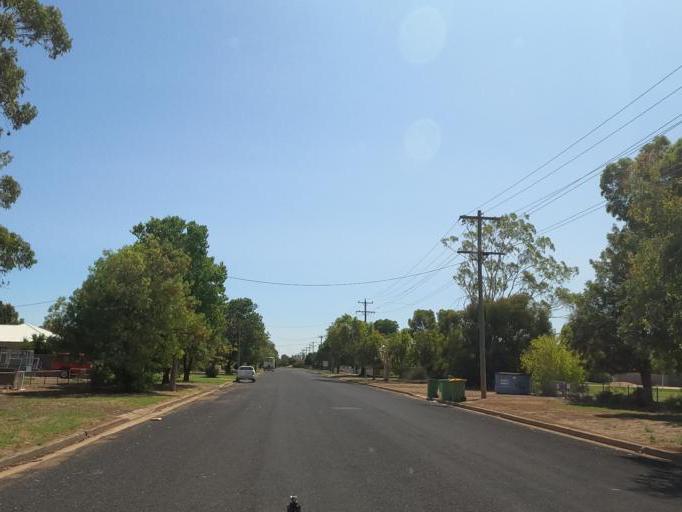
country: AU
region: New South Wales
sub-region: Corowa Shire
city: Mulwala
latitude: -35.9870
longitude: 146.0057
